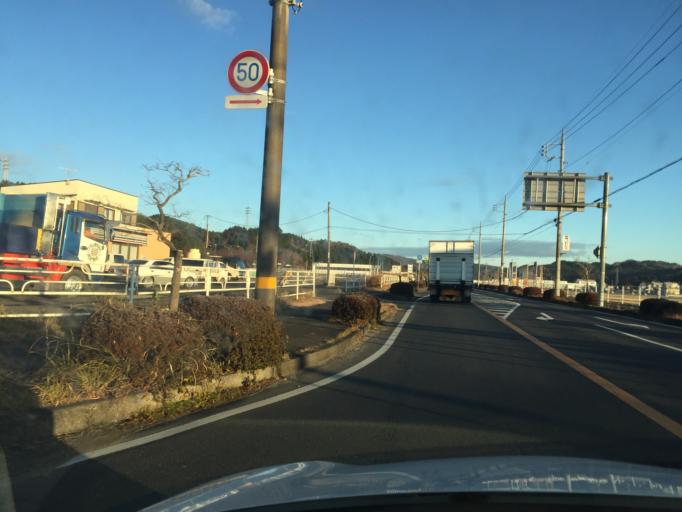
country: JP
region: Ibaraki
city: Kitaibaraki
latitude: 36.7934
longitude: 140.7284
